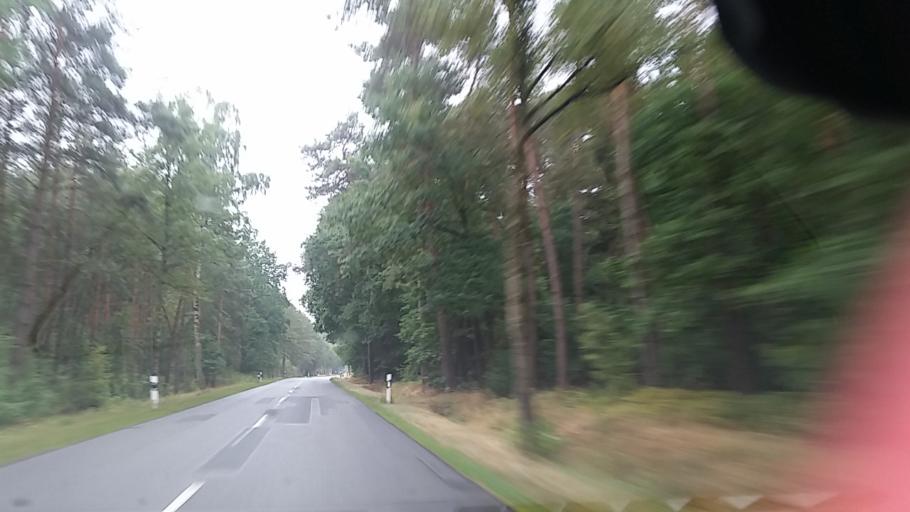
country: DE
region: Lower Saxony
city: Schoneworde
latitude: 52.6365
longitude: 10.6947
